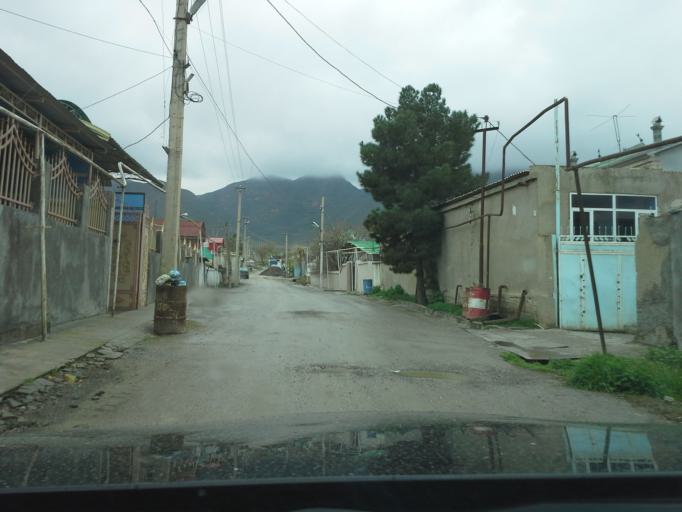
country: TM
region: Ahal
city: Abadan
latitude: 37.9575
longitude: 58.2027
